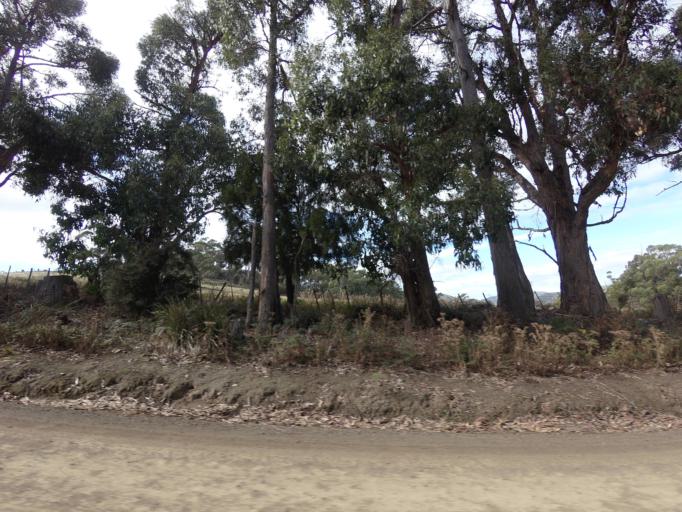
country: AU
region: Tasmania
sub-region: Clarence
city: Sandford
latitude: -43.0904
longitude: 147.7148
